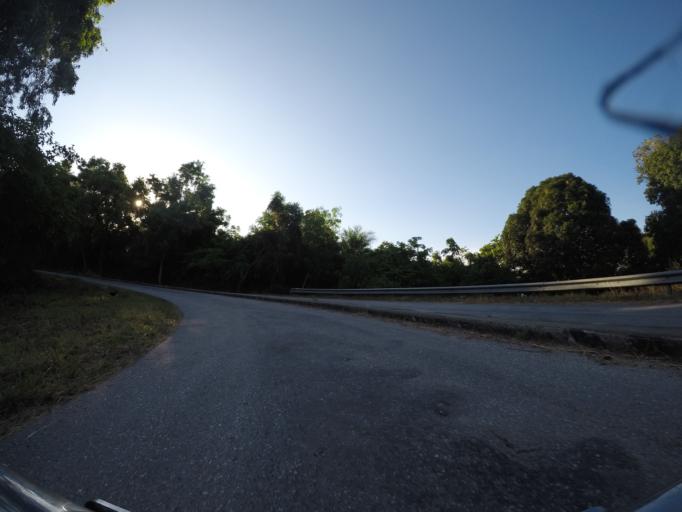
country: TZ
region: Pemba South
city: Mtambile
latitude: -5.3784
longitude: 39.6805
